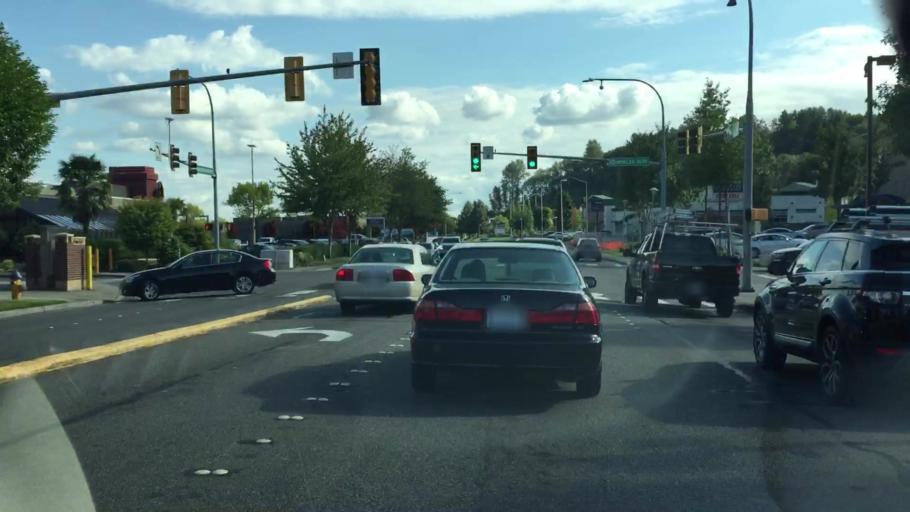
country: US
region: Washington
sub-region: King County
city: Tukwila
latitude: 47.4490
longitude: -122.2625
